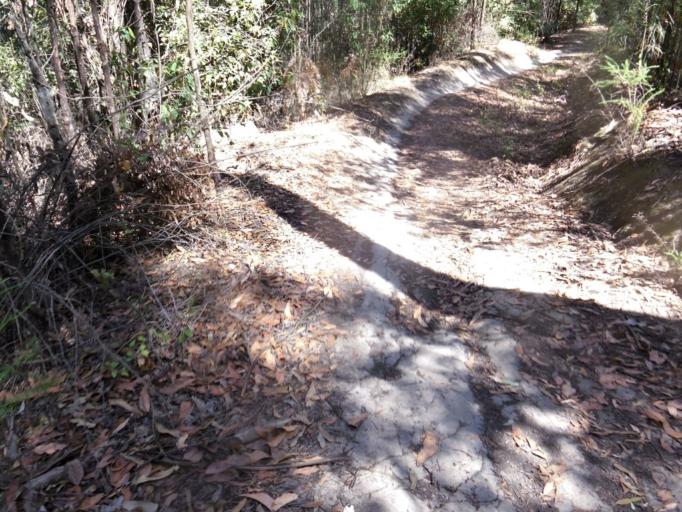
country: AU
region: Victoria
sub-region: Nillumbik
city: Saint Andrews
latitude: -37.5201
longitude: 145.3085
